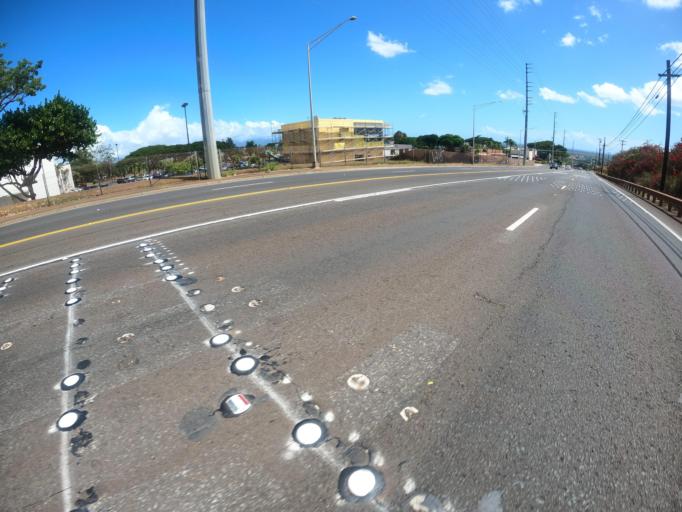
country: US
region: Hawaii
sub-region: Honolulu County
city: Royal Kunia
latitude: 21.3892
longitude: -158.0349
